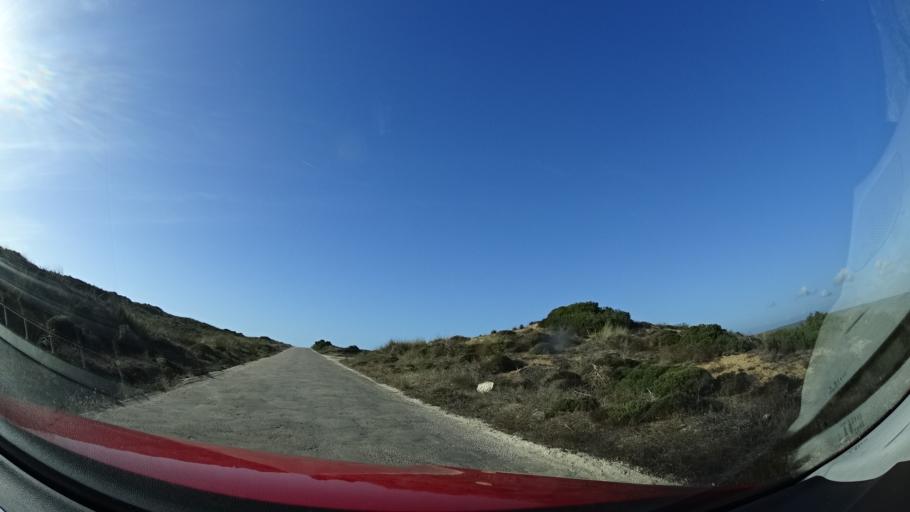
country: PT
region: Faro
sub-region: Vila do Bispo
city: Vila do Bispo
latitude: 37.1938
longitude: -8.9057
